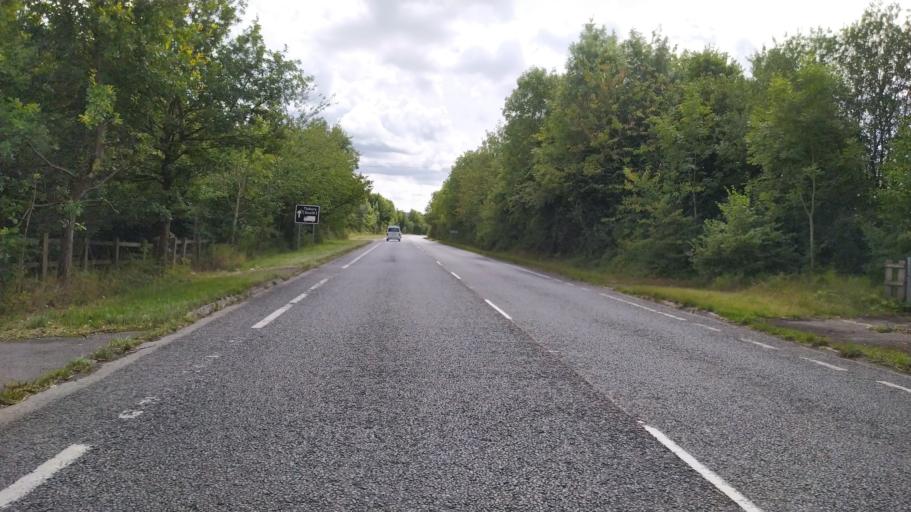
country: GB
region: England
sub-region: Wiltshire
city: Hindon
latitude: 51.0722
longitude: -2.1682
